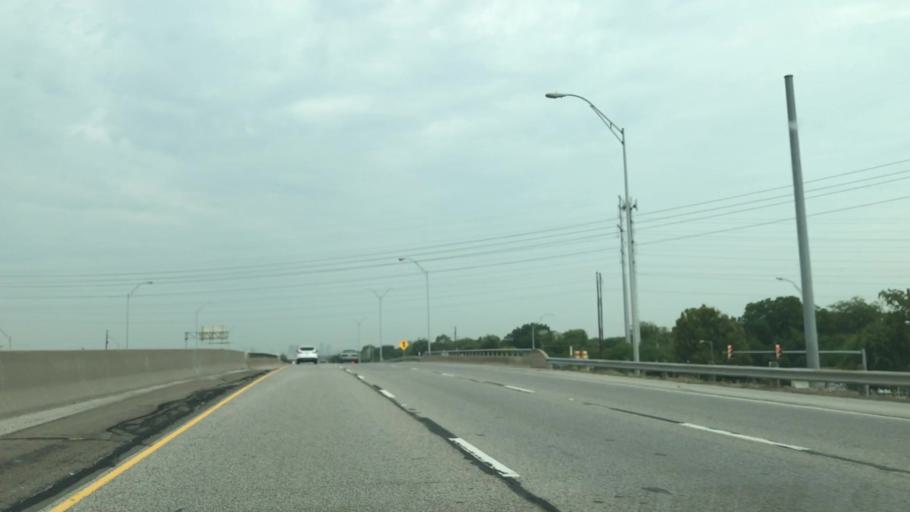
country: US
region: Texas
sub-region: Tarrant County
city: Richland Hills
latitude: 32.8016
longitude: -97.2206
